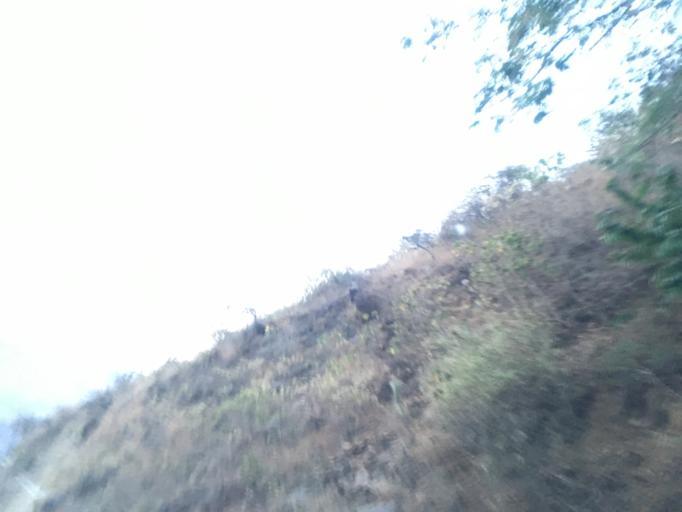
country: CO
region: Santander
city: Aratoca
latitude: 6.7922
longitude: -72.9978
